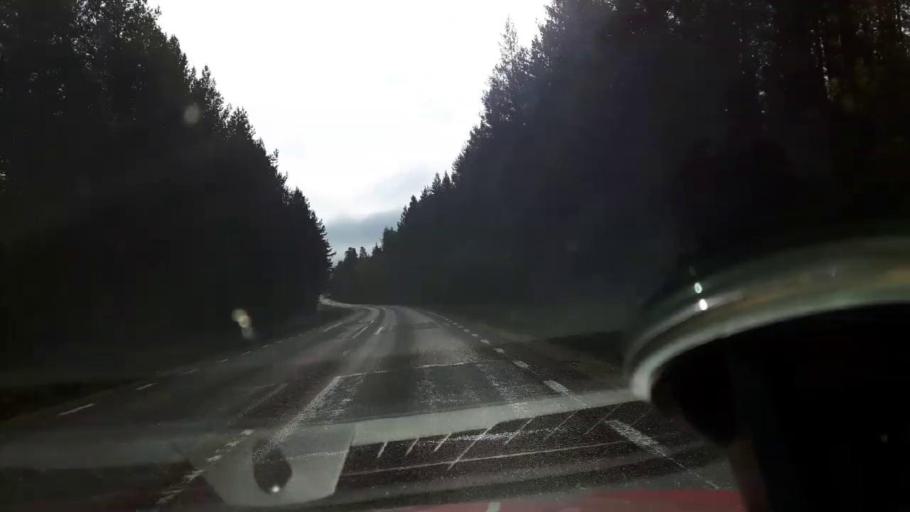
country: SE
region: Gaevleborg
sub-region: Ljusdals Kommun
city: Farila
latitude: 61.8813
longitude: 15.7101
